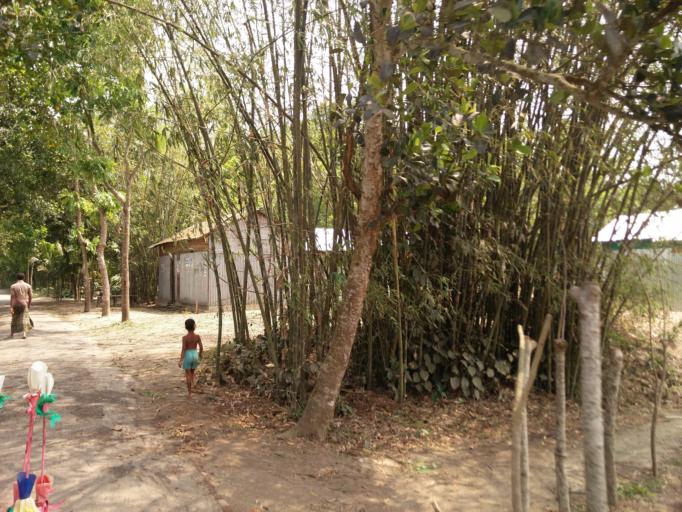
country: BD
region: Dhaka
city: Sherpur
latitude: 24.9338
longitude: 90.1604
